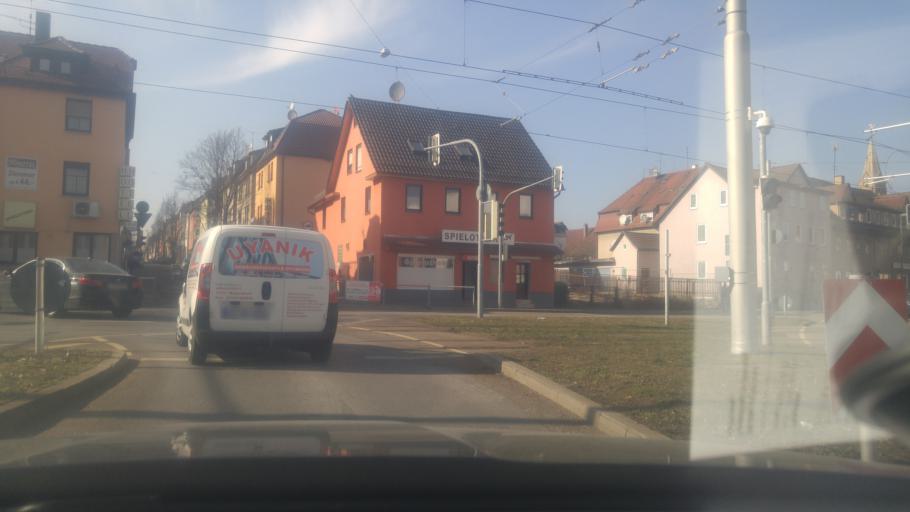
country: DE
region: Baden-Wuerttemberg
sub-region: Regierungsbezirk Stuttgart
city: Stuttgart Feuerbach
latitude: 48.8297
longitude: 9.1750
